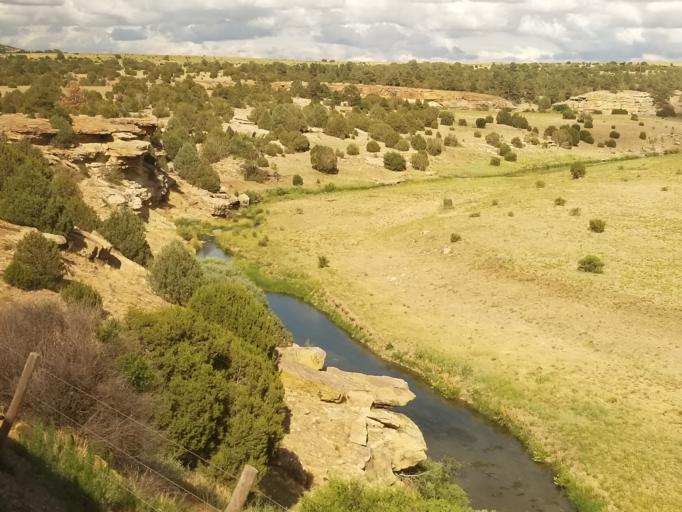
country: US
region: New Mexico
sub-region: San Miguel County
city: Las Vegas
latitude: 35.5548
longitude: -105.2146
